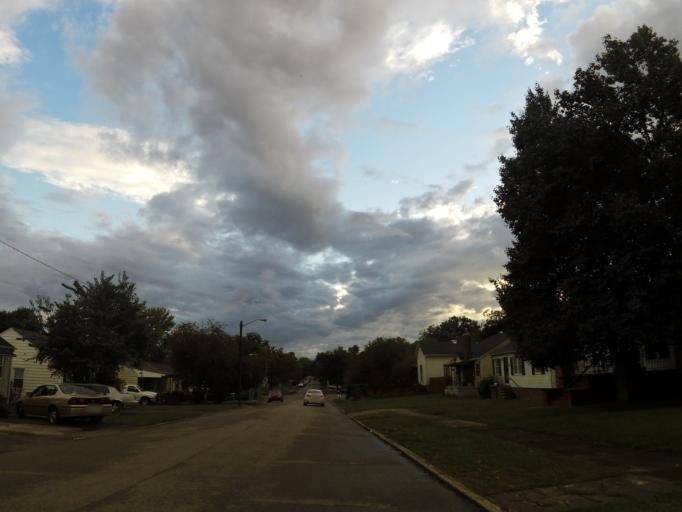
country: US
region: Tennessee
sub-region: Knox County
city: Knoxville
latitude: 35.9893
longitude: -83.8947
